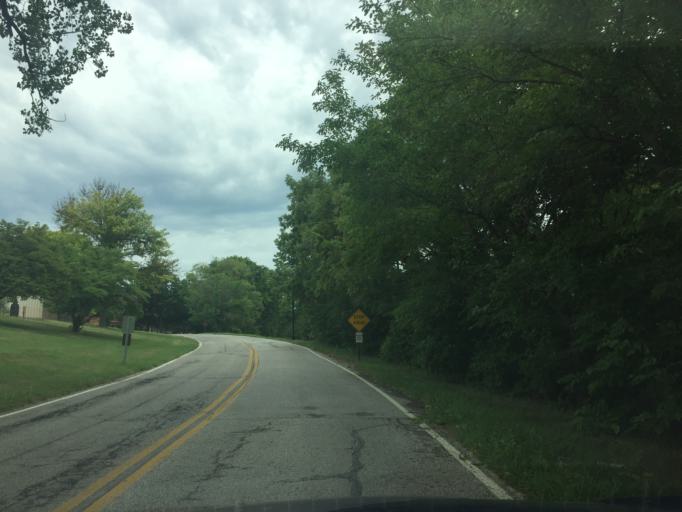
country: US
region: Kansas
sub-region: Leavenworth County
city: Leavenworth
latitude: 39.3476
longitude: -94.9127
